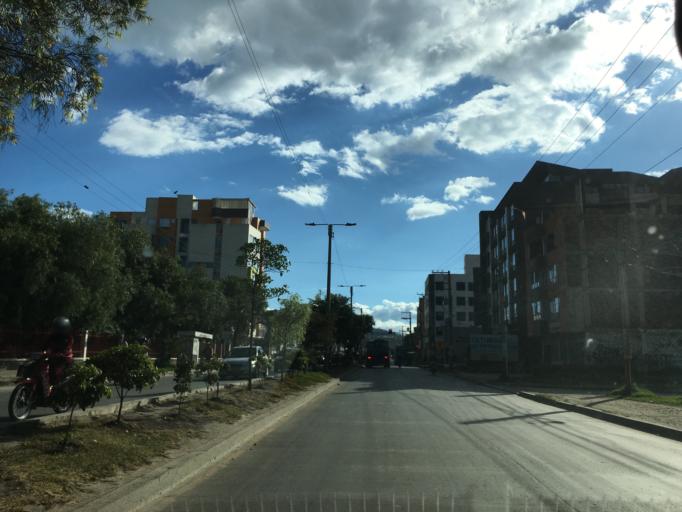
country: CO
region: Boyaca
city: Sogamoso
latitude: 5.7267
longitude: -72.9219
